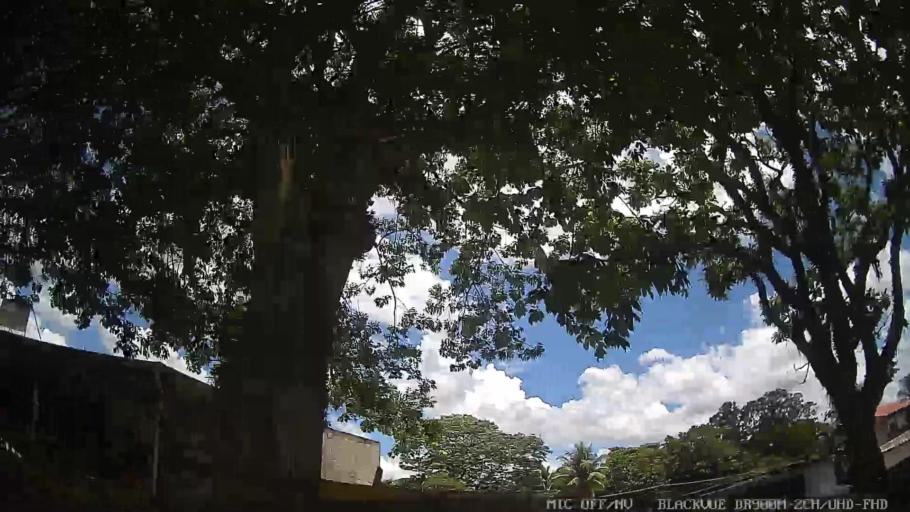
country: BR
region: Sao Paulo
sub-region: Jaguariuna
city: Jaguariuna
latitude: -22.7056
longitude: -46.9806
